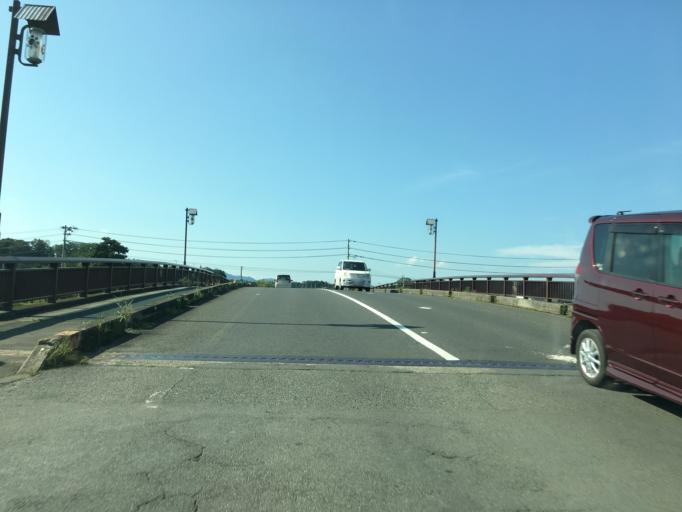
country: JP
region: Miyagi
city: Marumori
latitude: 37.7898
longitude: 140.9128
